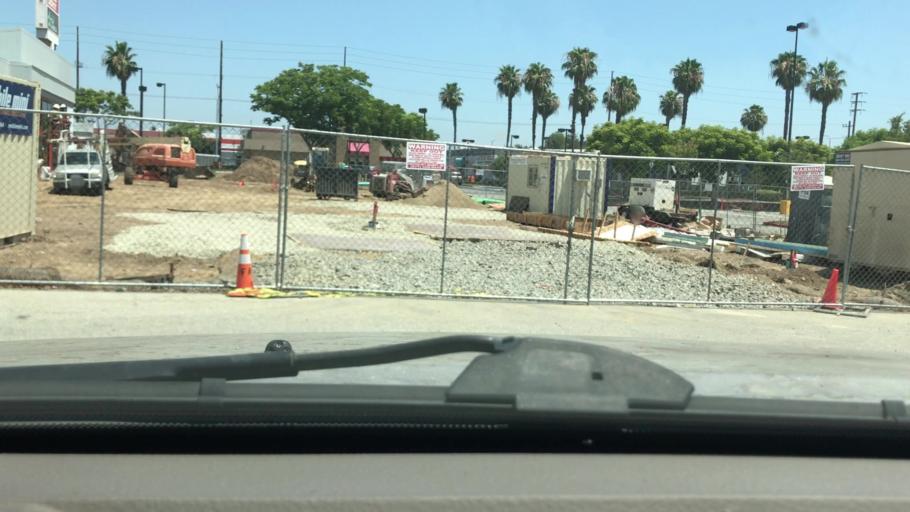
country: US
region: California
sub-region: Los Angeles County
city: Gardena
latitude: 33.8569
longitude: -118.3022
